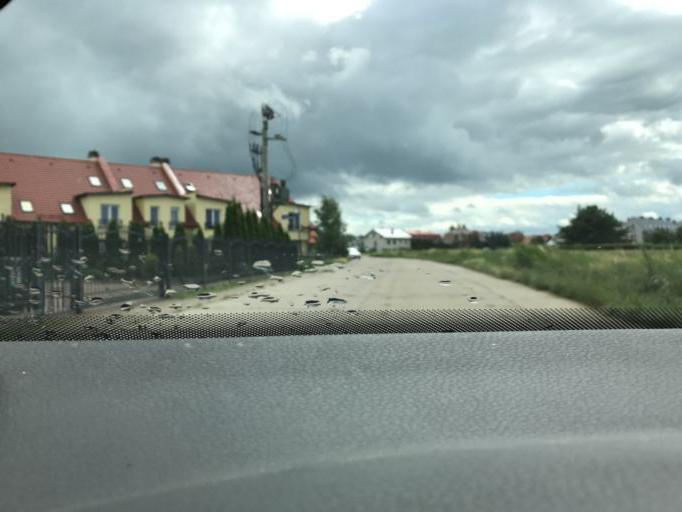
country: PL
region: Pomeranian Voivodeship
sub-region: Powiat gdanski
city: Pruszcz Gdanski
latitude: 54.2625
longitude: 18.6824
